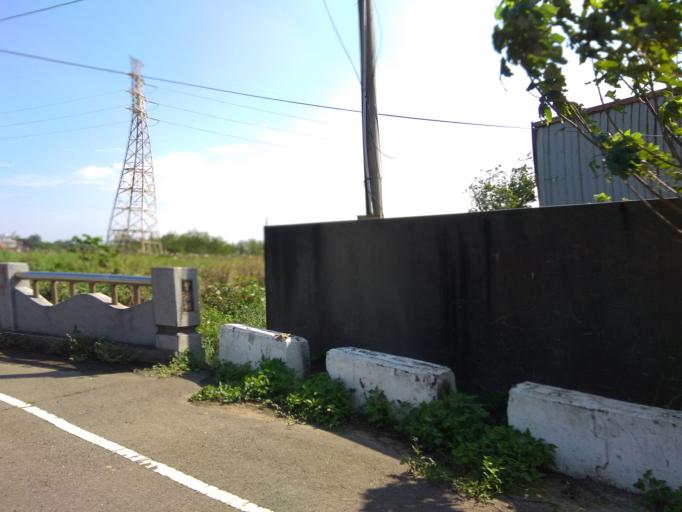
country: TW
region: Taiwan
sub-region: Hsinchu
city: Zhubei
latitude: 24.9858
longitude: 121.0349
